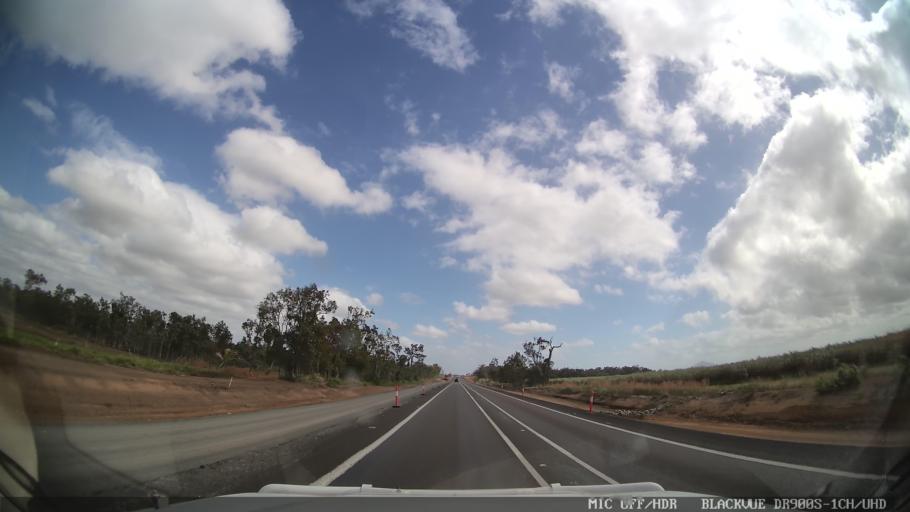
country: AU
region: Queensland
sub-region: Whitsunday
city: Red Hill
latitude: -20.2977
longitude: 148.5070
